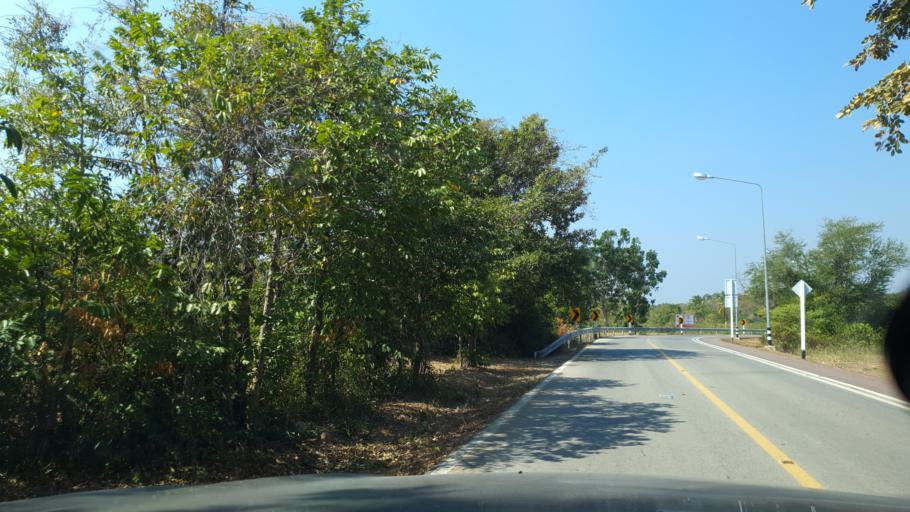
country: TH
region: Prachuap Khiri Khan
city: Sam Roi Yot
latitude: 12.2789
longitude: 99.9734
